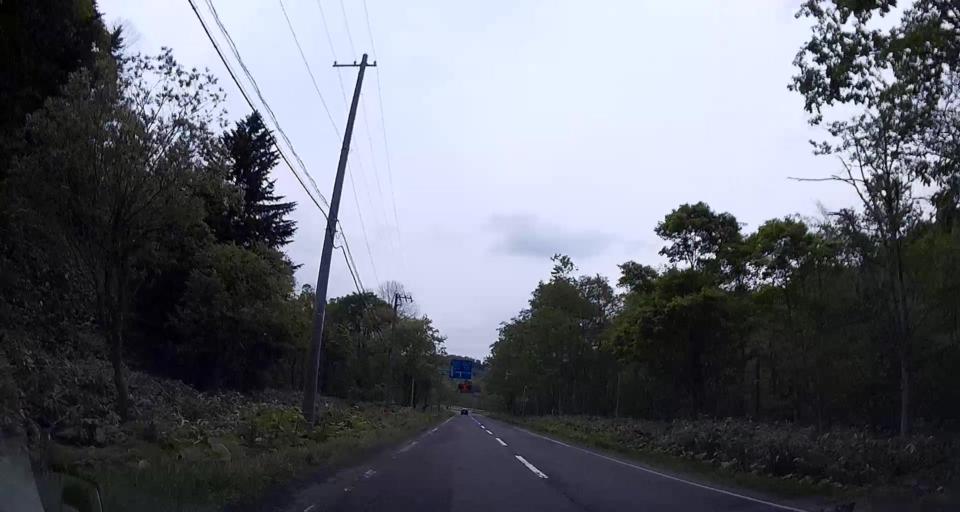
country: JP
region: Hokkaido
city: Shiraoi
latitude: 42.6914
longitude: 141.1054
